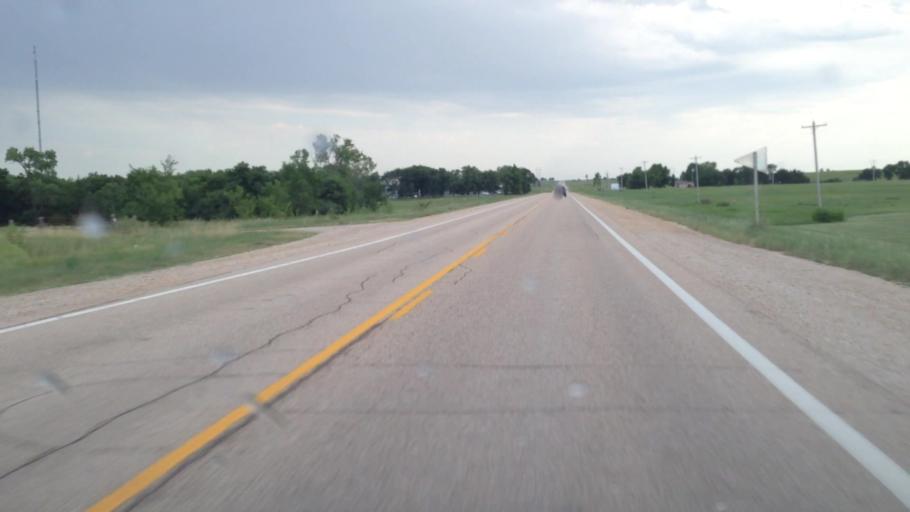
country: US
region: Kansas
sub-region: Coffey County
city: Burlington
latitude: 38.1692
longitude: -95.7389
